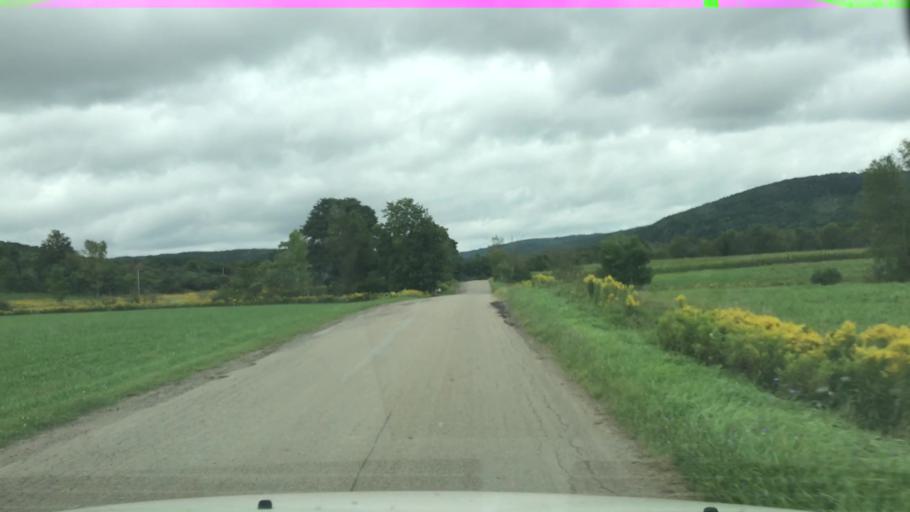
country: US
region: New York
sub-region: Cattaraugus County
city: Little Valley
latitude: 42.3180
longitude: -78.7223
